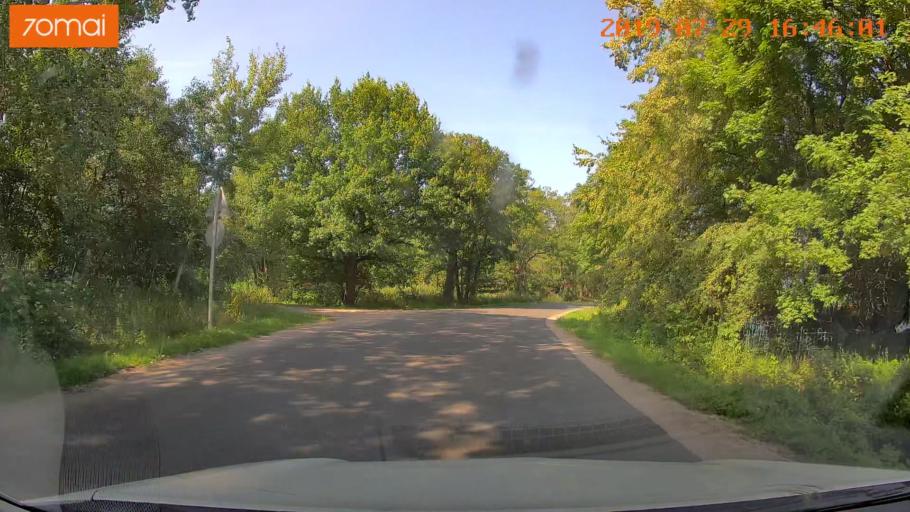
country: RU
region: Kaliningrad
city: Primorsk
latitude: 54.7703
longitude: 20.0802
